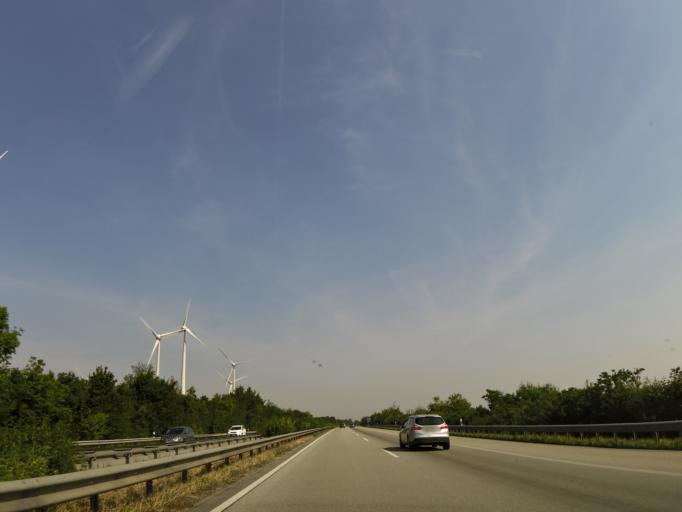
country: DE
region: Rheinland-Pfalz
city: Heuchelheim bei Frankenthal
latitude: 49.5800
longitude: 8.2950
